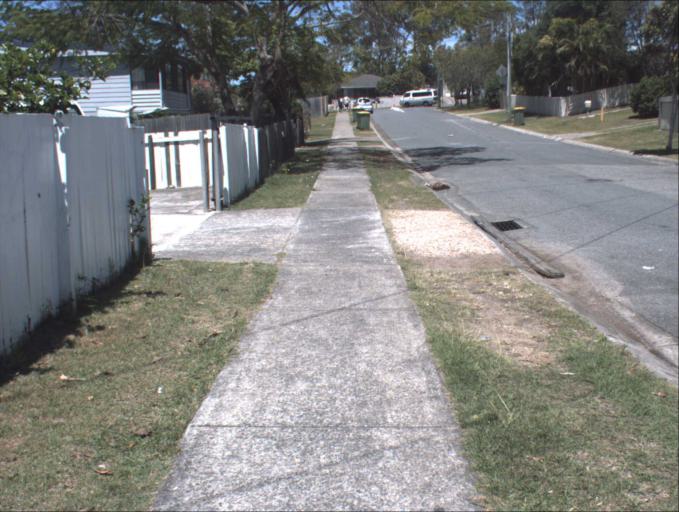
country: AU
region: Queensland
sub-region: Logan
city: Woodridge
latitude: -27.6303
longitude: 153.1067
